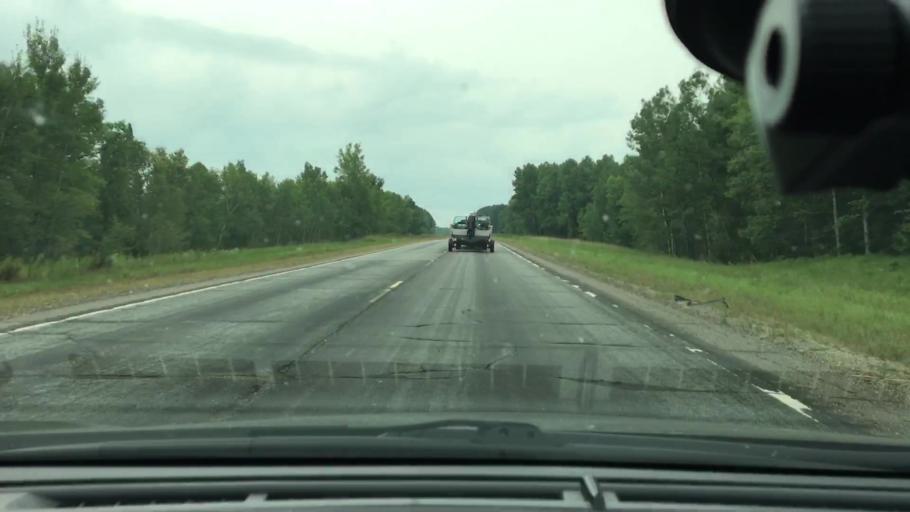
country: US
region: Minnesota
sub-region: Crow Wing County
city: Crosby
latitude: 46.6416
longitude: -93.9509
